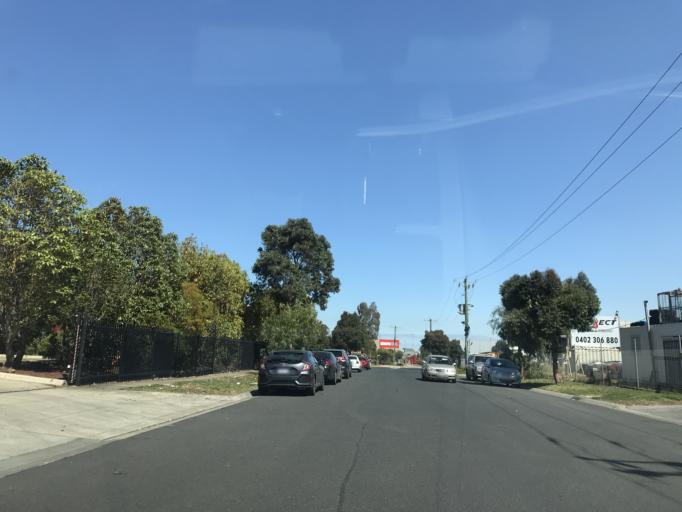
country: AU
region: Victoria
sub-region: Wyndham
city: Truganina
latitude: -37.8236
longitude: 144.7717
